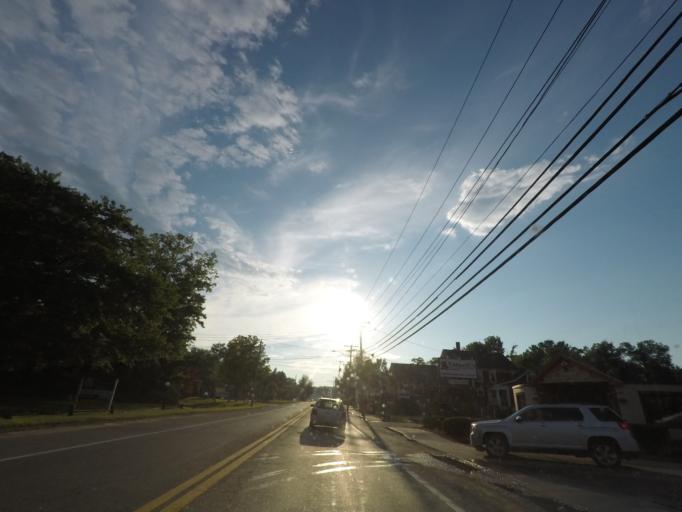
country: US
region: Massachusetts
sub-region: Worcester County
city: Fiskdale
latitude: 42.1134
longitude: -72.1019
